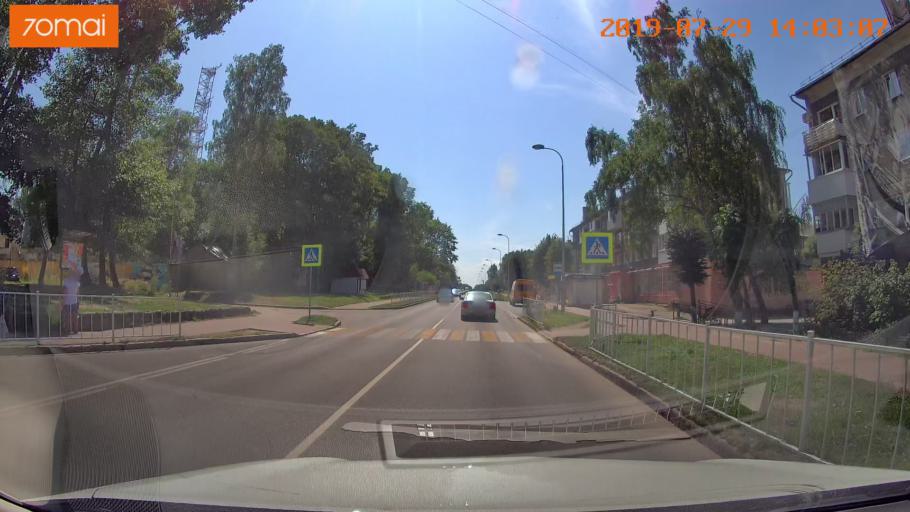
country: RU
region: Kaliningrad
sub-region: Gorod Kaliningrad
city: Baltiysk
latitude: 54.6597
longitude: 19.9143
